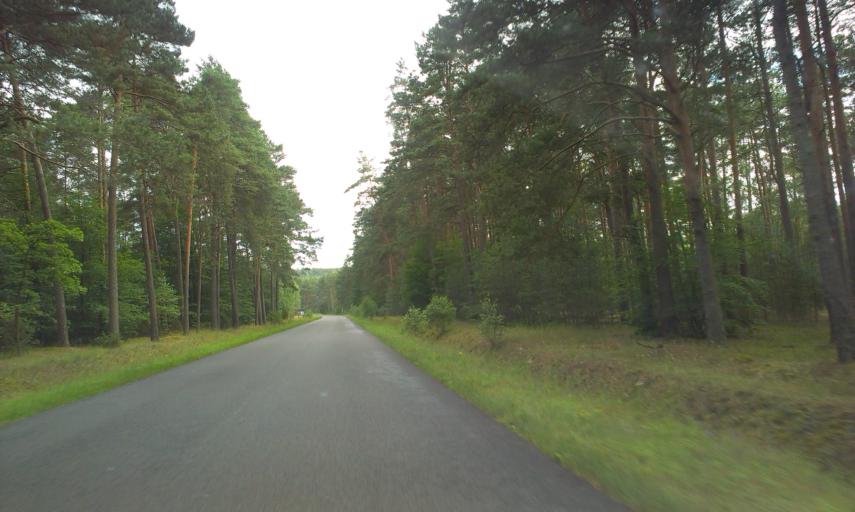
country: PL
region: Greater Poland Voivodeship
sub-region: Powiat zlotowski
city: Okonek
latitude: 53.4966
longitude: 16.9822
